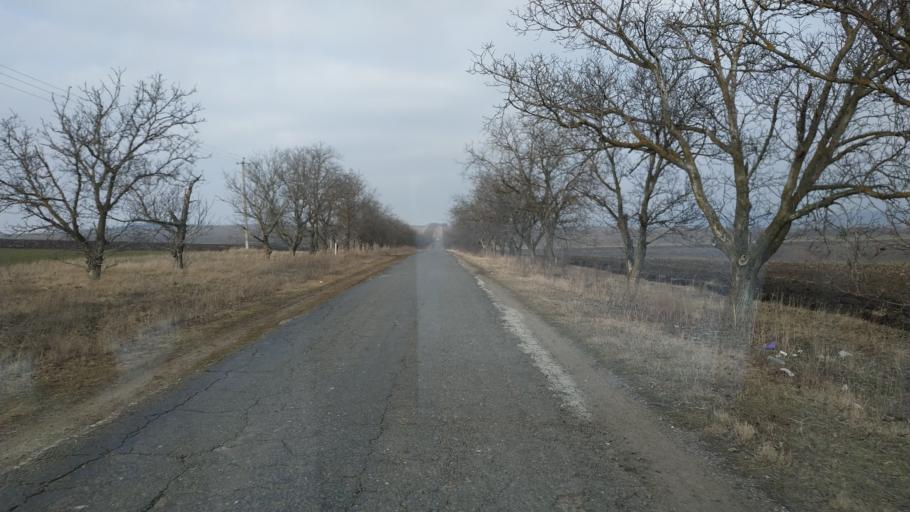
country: MD
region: Hincesti
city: Dancu
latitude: 46.8688
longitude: 28.2937
